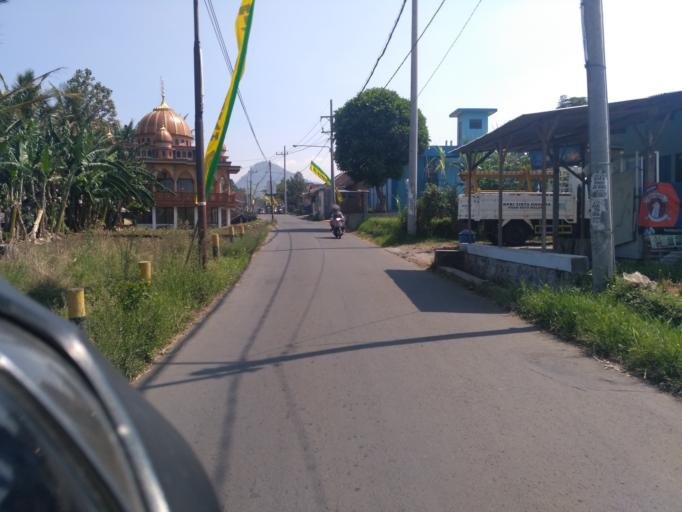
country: ID
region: East Java
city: Batu
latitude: -7.9055
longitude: 112.5834
